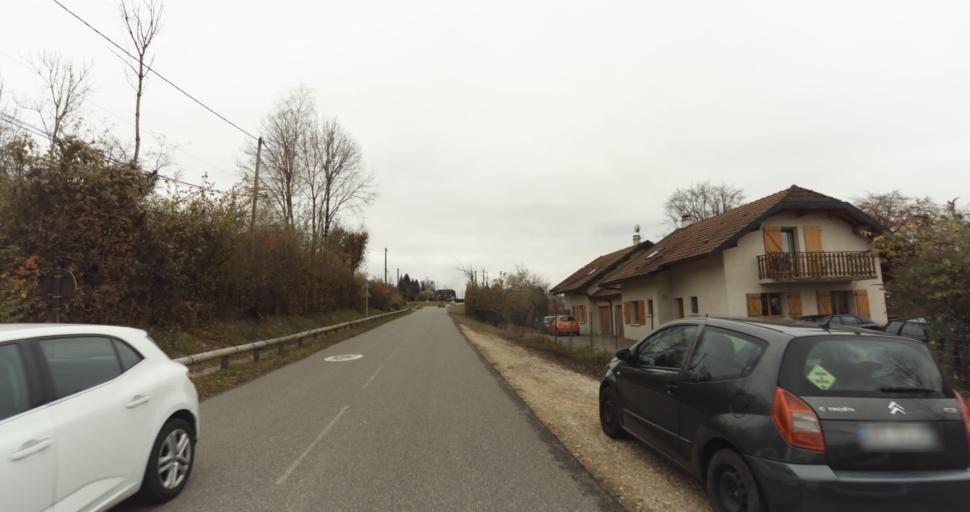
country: FR
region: Rhone-Alpes
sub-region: Departement de la Haute-Savoie
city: Saint-Martin-Bellevue
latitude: 45.9619
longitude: 6.1444
